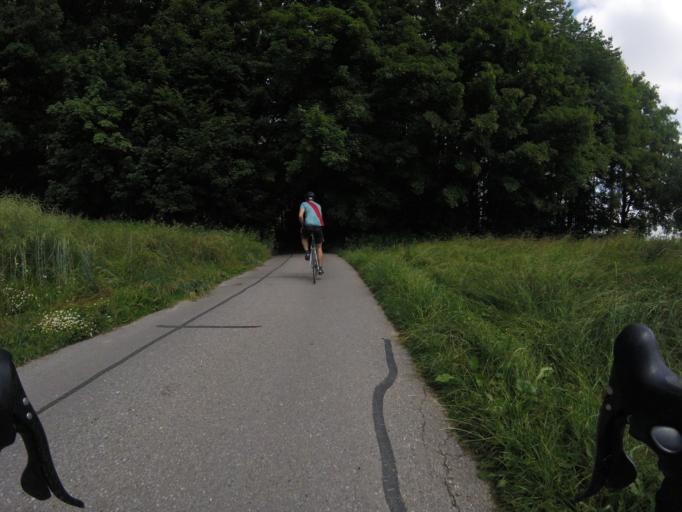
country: CH
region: Bern
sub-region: Bern-Mittelland District
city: Bariswil
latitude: 47.0181
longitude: 7.5169
